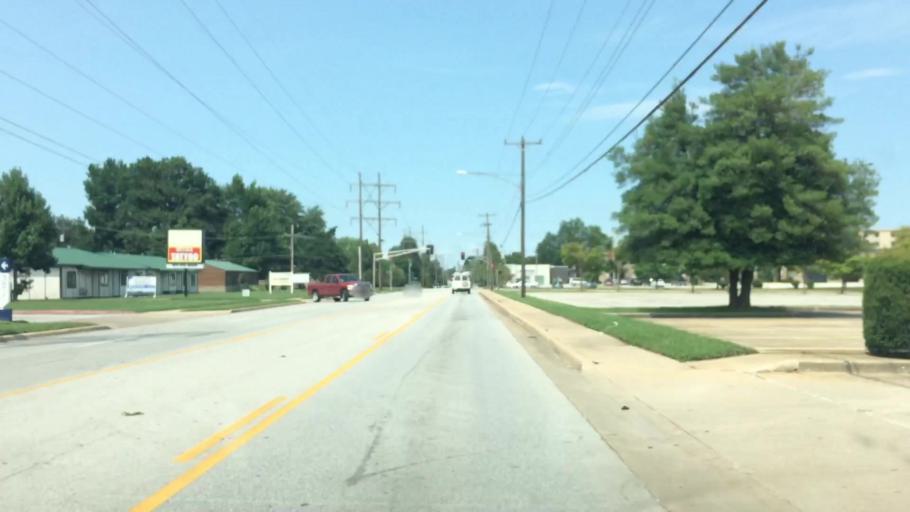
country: US
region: Missouri
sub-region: Greene County
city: Springfield
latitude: 37.1614
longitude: -93.2717
